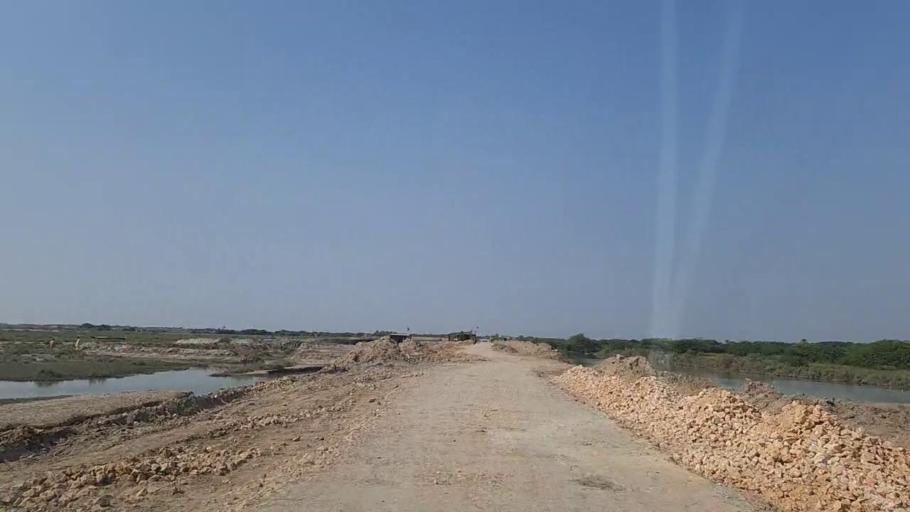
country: PK
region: Sindh
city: Chuhar Jamali
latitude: 24.1946
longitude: 67.8389
